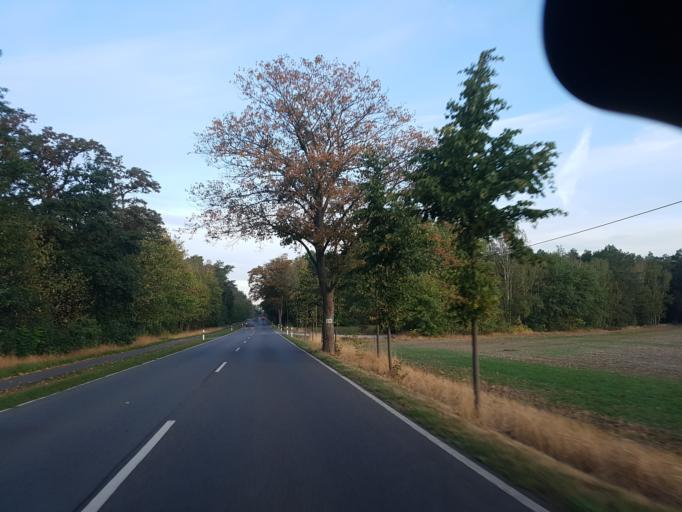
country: DE
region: Brandenburg
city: Finsterwalde
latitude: 51.6517
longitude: 13.6785
